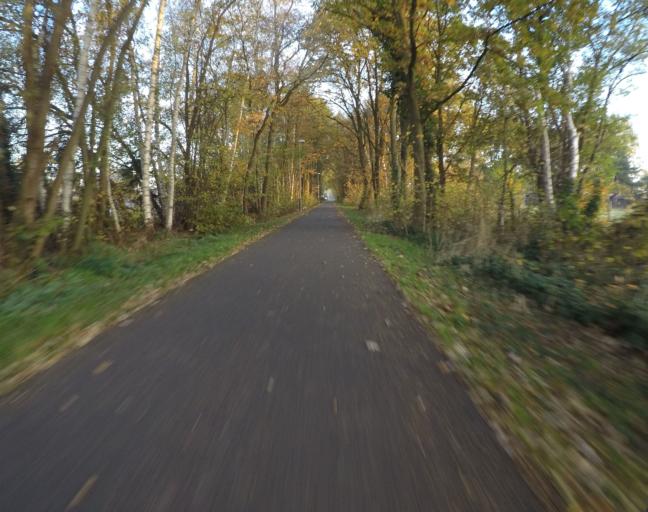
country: BE
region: Flanders
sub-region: Provincie Antwerpen
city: Hulshout
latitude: 51.0684
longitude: 4.8252
